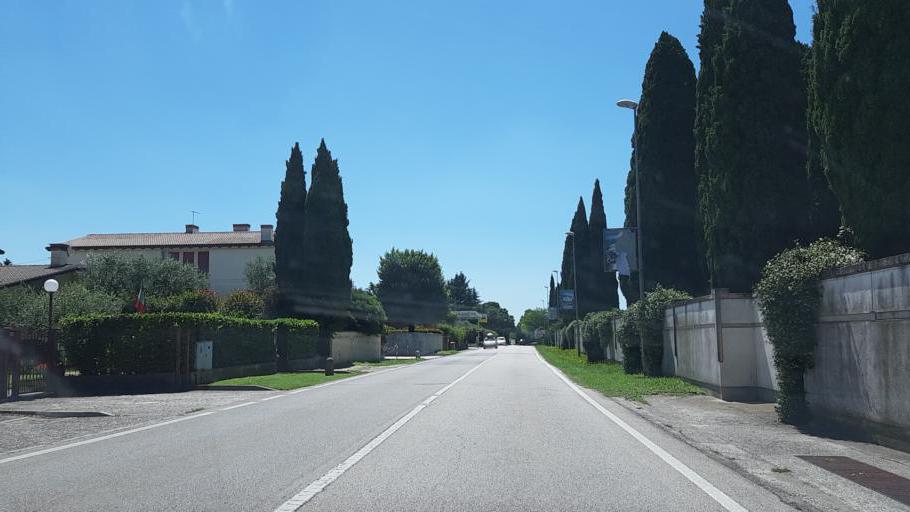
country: IT
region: Veneto
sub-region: Provincia di Vicenza
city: Pove del Grappa
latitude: 45.7819
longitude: 11.7402
